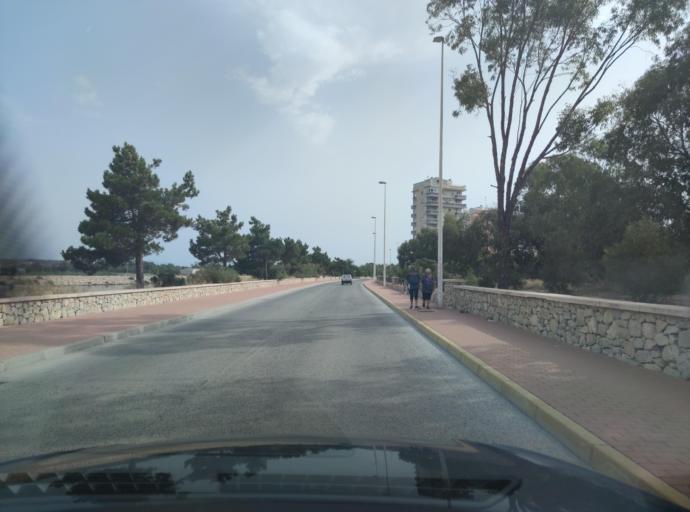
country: ES
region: Valencia
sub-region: Provincia de Alicante
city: Guardamar del Segura
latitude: 38.1071
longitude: -0.6535
